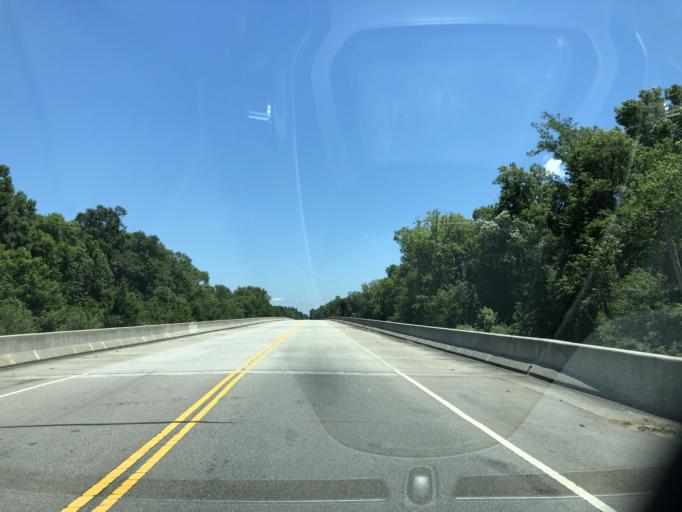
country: US
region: South Carolina
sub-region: Orangeburg County
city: Branchville
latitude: 33.2408
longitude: -80.8576
